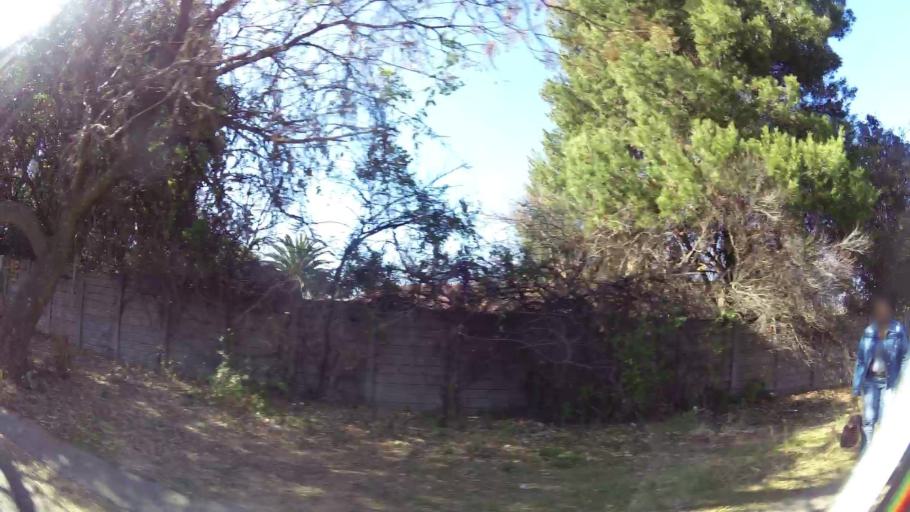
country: ZA
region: Gauteng
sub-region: Ekurhuleni Metropolitan Municipality
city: Germiston
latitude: -26.3320
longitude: 28.1052
